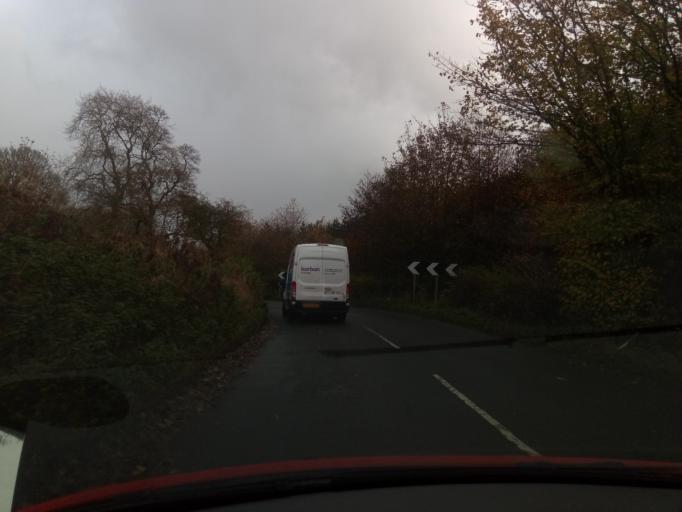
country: GB
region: England
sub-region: Northumberland
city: Birtley
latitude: 55.0552
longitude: -2.1760
